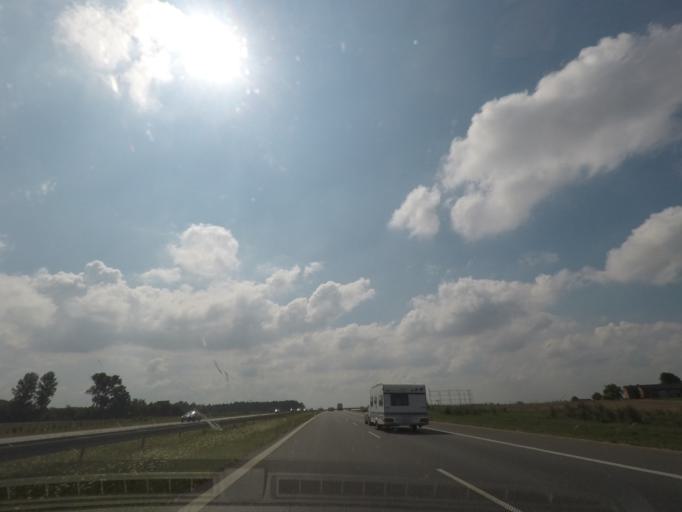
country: PL
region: Lodz Voivodeship
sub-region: Powiat kutnowski
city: Krzyzanow
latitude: 52.1991
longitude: 19.4859
